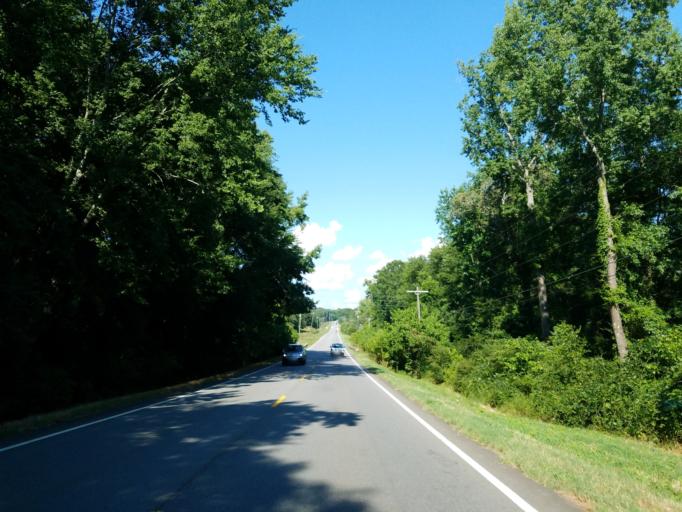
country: US
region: Georgia
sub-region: Peach County
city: Fort Valley
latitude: 32.5544
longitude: -83.8626
